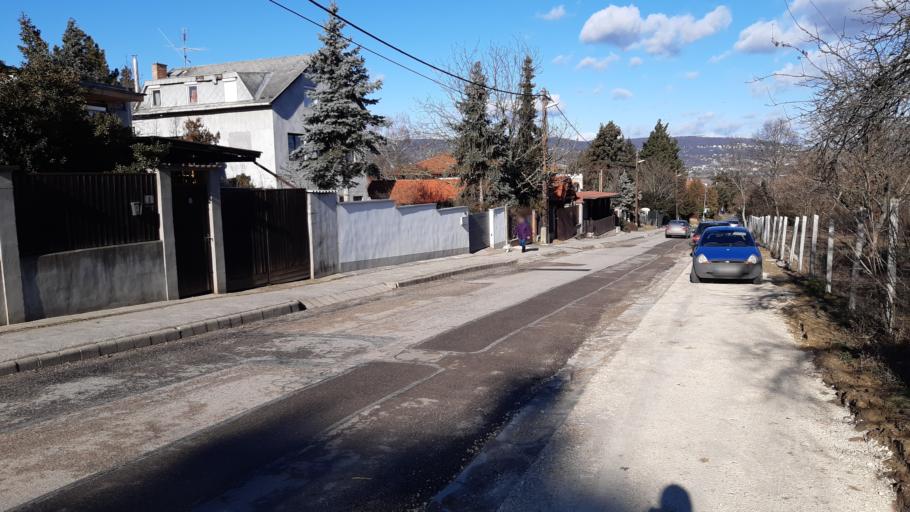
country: HU
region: Pest
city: Budaors
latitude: 47.4343
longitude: 18.9783
